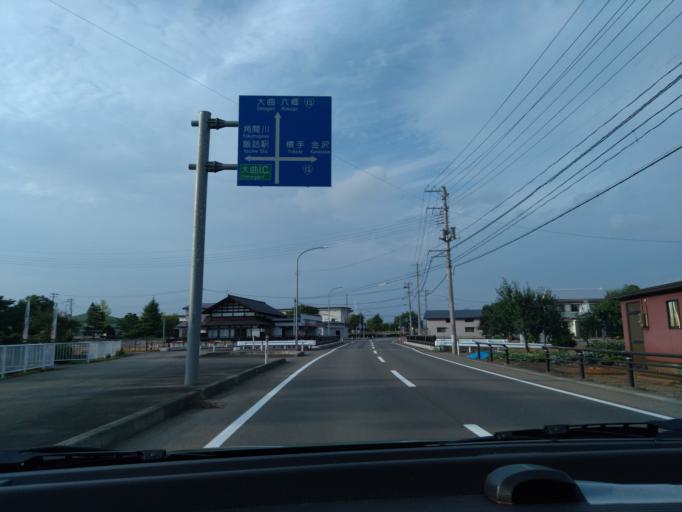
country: JP
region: Akita
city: Yokotemachi
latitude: 39.3850
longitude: 140.5307
